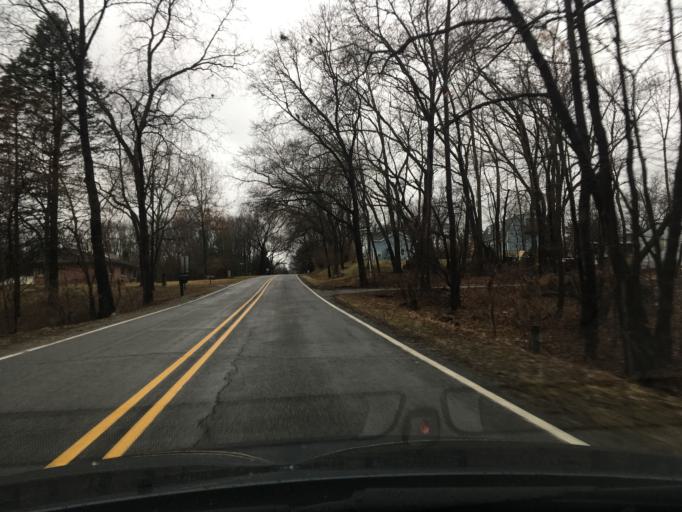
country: US
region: Michigan
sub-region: Washtenaw County
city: Chelsea
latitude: 42.3102
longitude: -84.1119
